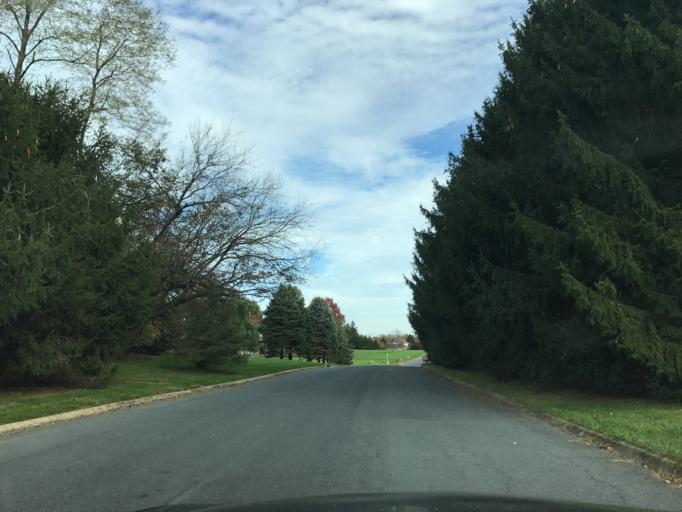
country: US
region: Maryland
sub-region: Harford County
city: Pleasant Hills
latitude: 39.4833
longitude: -76.3791
